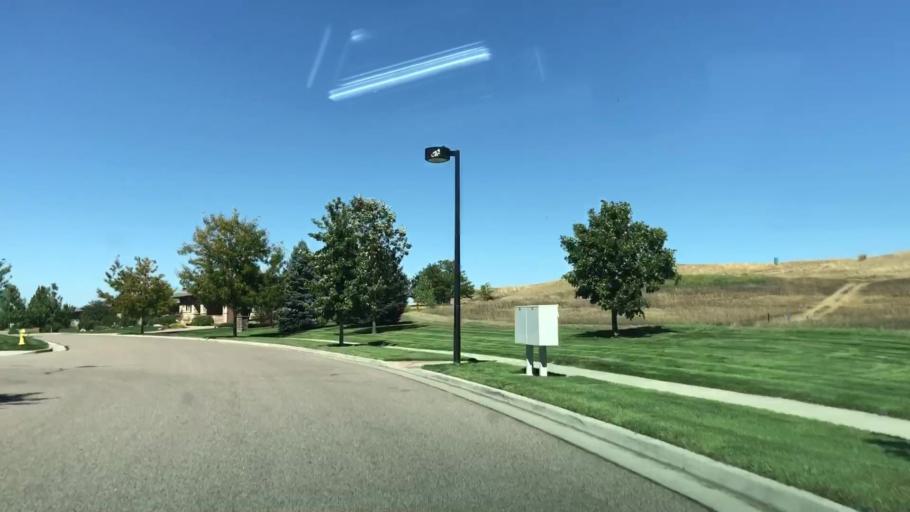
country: US
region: Colorado
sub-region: Weld County
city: Windsor
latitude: 40.5341
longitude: -104.9573
